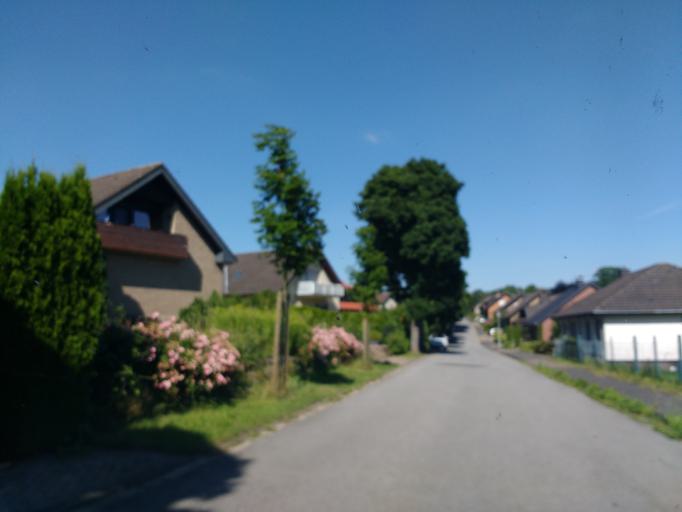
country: DE
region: North Rhine-Westphalia
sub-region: Regierungsbezirk Detmold
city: Schlangen
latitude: 51.8267
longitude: 8.8574
